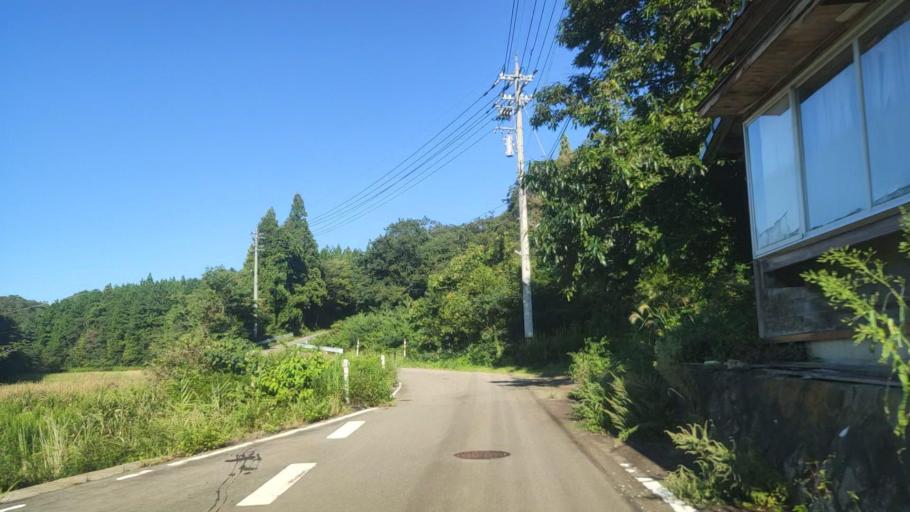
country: JP
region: Ishikawa
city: Nanao
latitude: 37.1159
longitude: 136.8845
